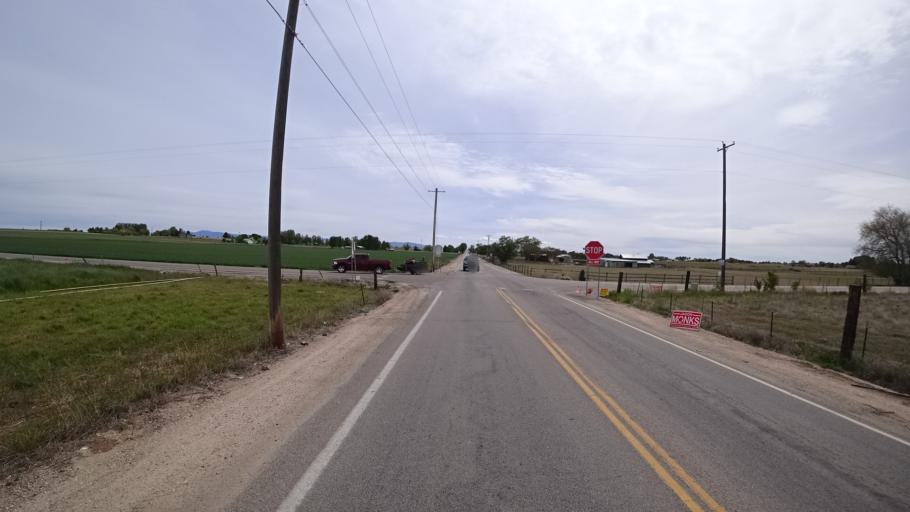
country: US
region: Idaho
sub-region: Ada County
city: Kuna
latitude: 43.5612
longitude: -116.4539
